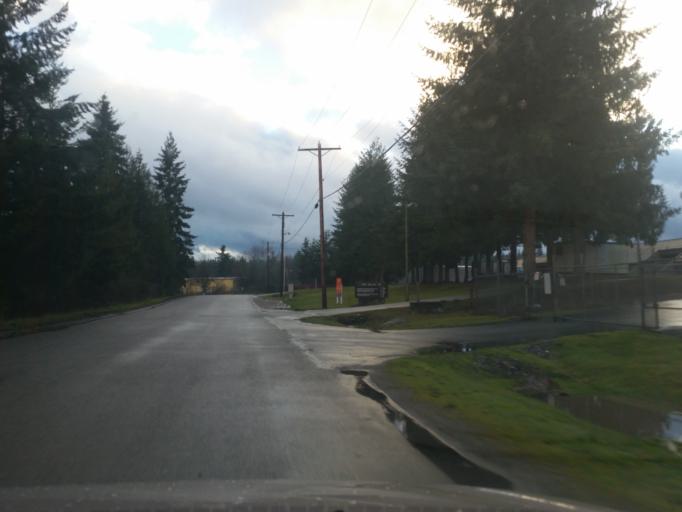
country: US
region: Washington
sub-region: Snohomish County
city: Maltby
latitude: 47.7996
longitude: -122.1171
